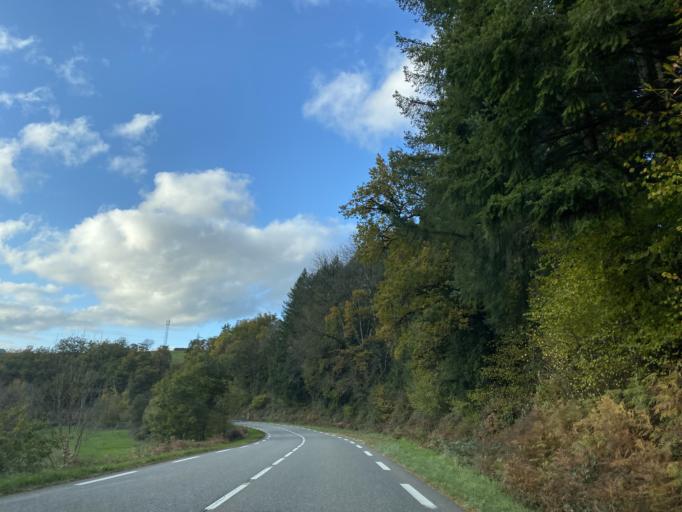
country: FR
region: Auvergne
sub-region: Departement du Puy-de-Dome
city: Job
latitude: 45.6481
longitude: 3.6790
